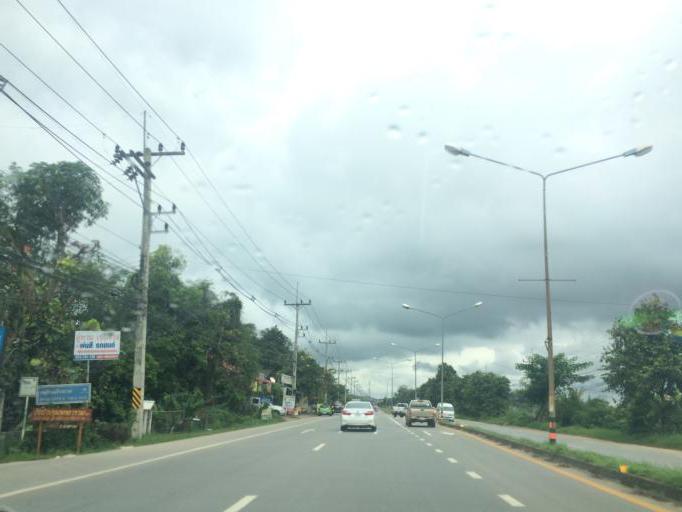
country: TH
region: Chiang Rai
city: Mae Chan
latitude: 20.0313
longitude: 99.8739
